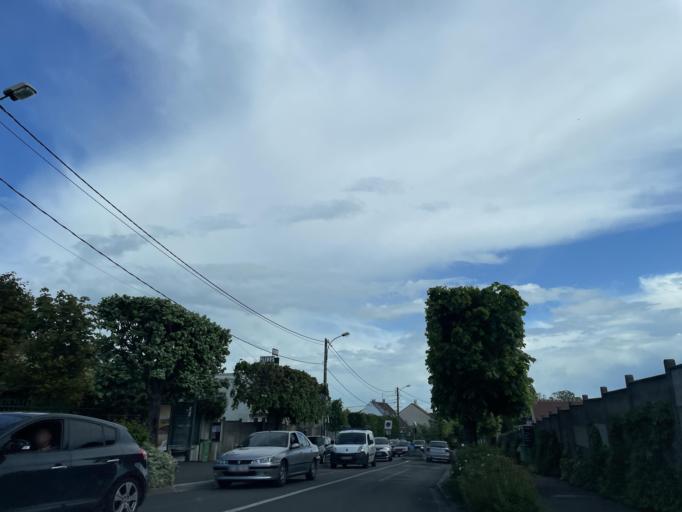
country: FR
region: Ile-de-France
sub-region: Departement du Val-d'Oise
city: Arnouville
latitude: 48.9828
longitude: 2.4207
